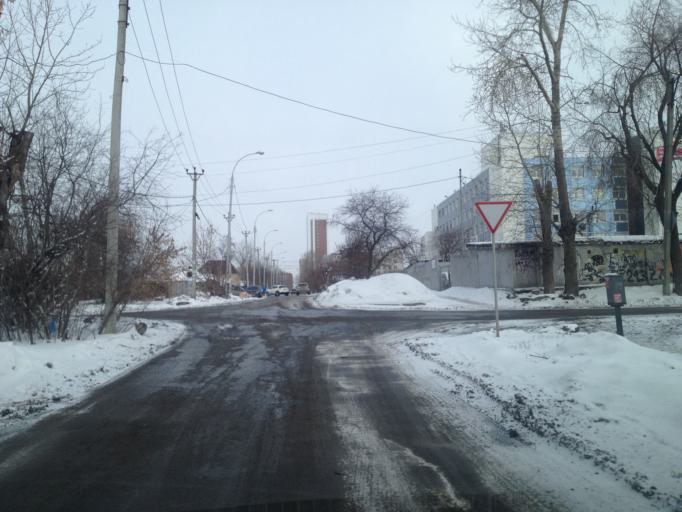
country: RU
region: Sverdlovsk
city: Yekaterinburg
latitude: 56.8011
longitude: 60.5979
